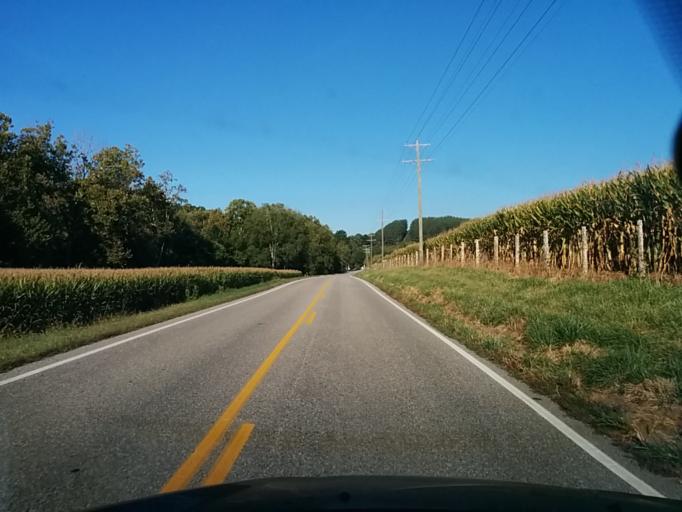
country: US
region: Virginia
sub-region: City of Lexington
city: Lexington
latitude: 37.7458
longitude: -79.5208
